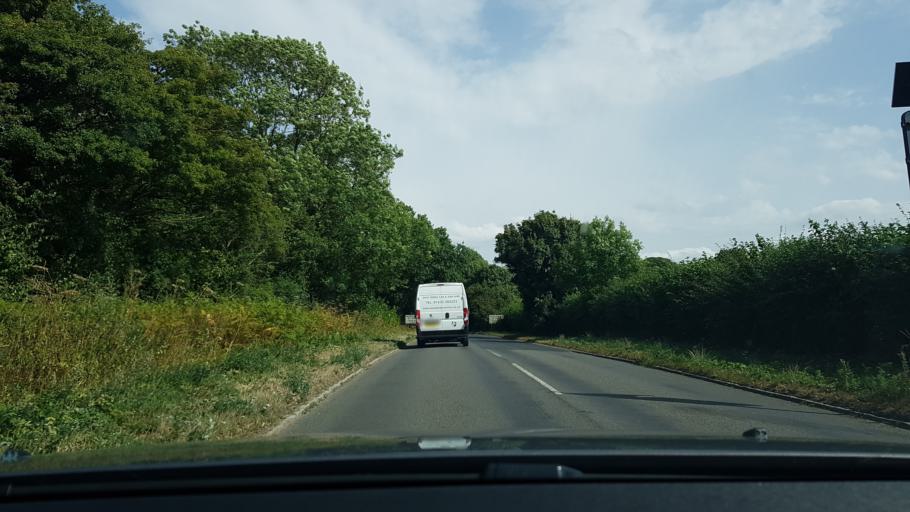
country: GB
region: England
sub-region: West Berkshire
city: Lambourn
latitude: 51.4746
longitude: -1.5242
